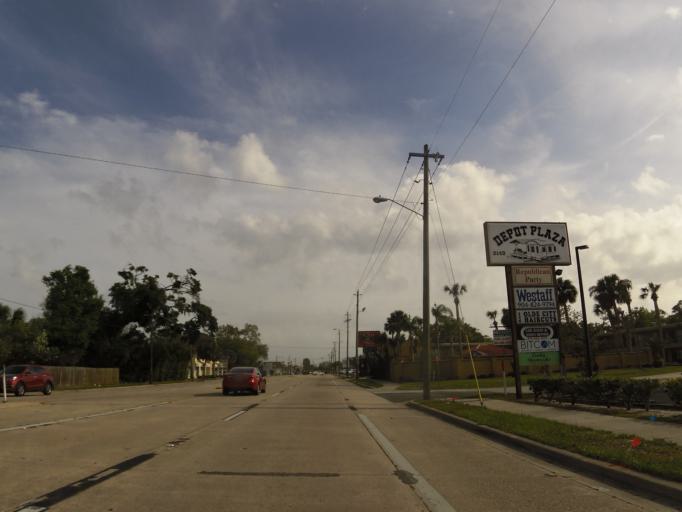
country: US
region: Florida
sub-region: Saint Johns County
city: Saint Augustine
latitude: 29.9204
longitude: -81.3252
